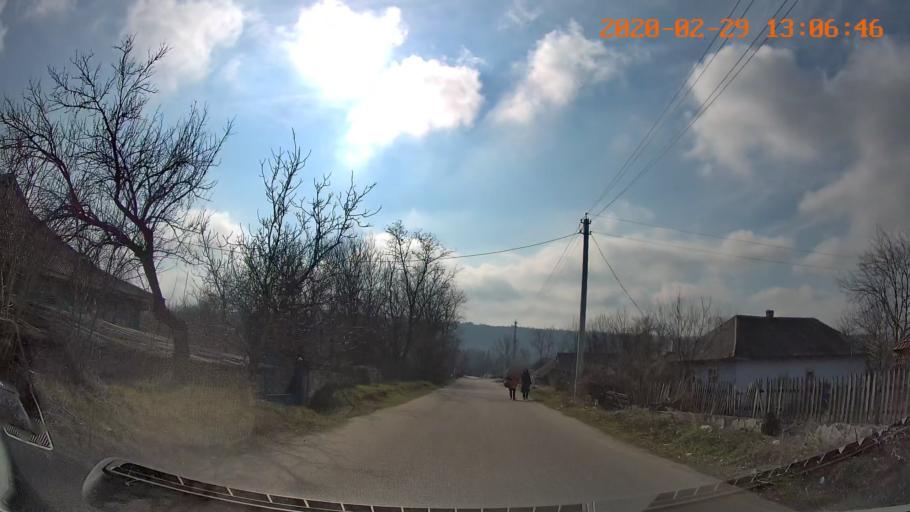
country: MD
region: Telenesti
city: Camenca
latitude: 48.0114
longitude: 28.7067
